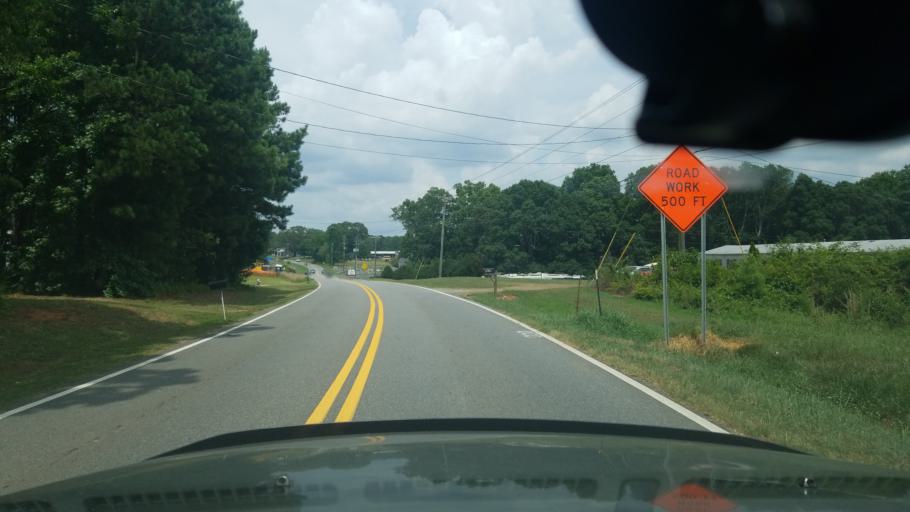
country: US
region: Georgia
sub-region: Fulton County
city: Milton
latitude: 34.2386
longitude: -84.2562
